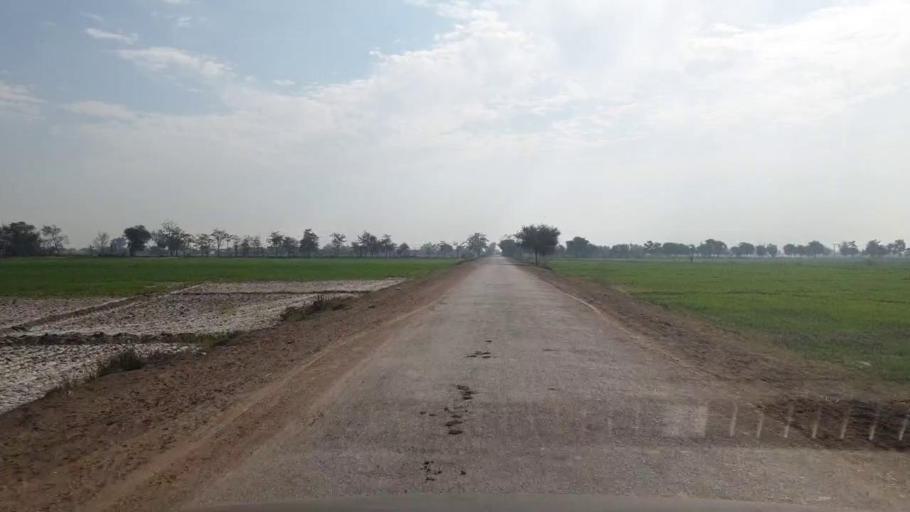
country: PK
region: Sindh
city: Hala
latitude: 25.9964
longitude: 68.4149
